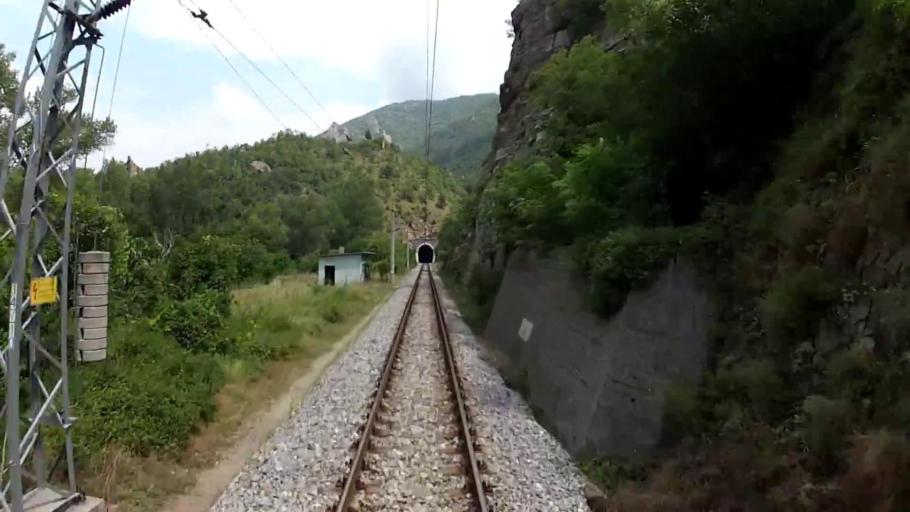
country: BG
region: Blagoevgrad
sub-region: Obshtina Kresna
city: Stara Kresna
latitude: 41.8234
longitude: 23.1594
